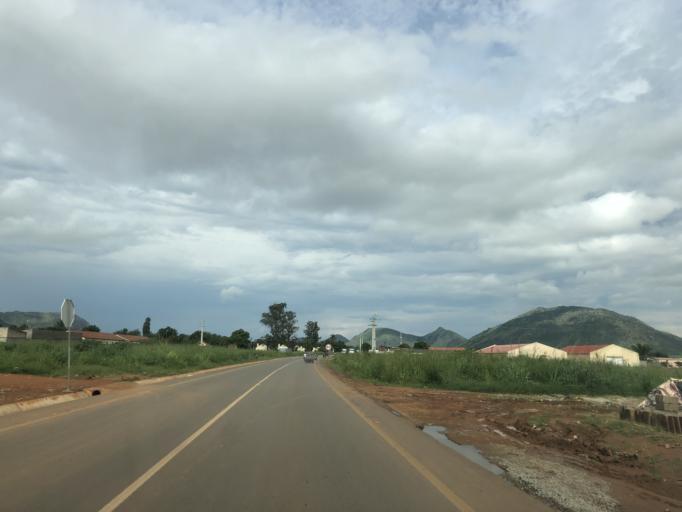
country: AO
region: Cuanza Sul
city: Uacu Cungo
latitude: -11.3516
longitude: 15.1122
